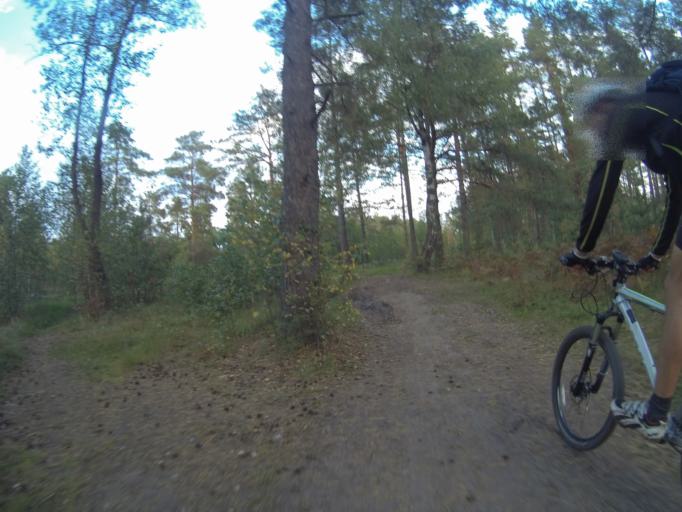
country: RU
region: Vladimir
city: Sobinka
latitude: 55.9755
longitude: 40.0088
